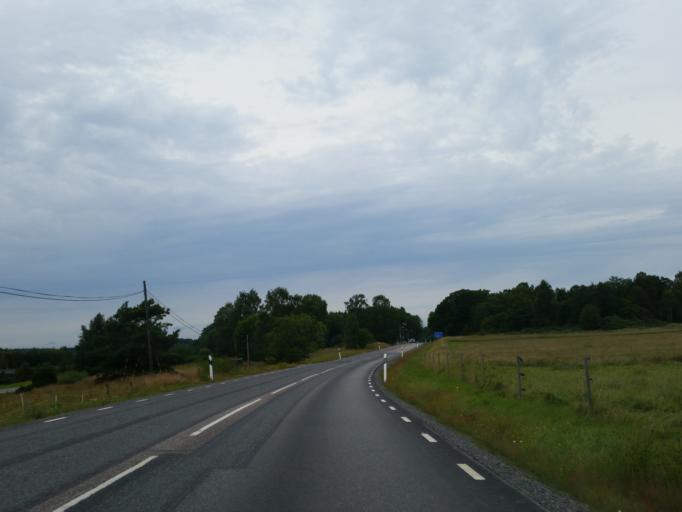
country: SE
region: Stockholm
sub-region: Nykvarns Kommun
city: Nykvarn
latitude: 59.1900
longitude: 17.4652
